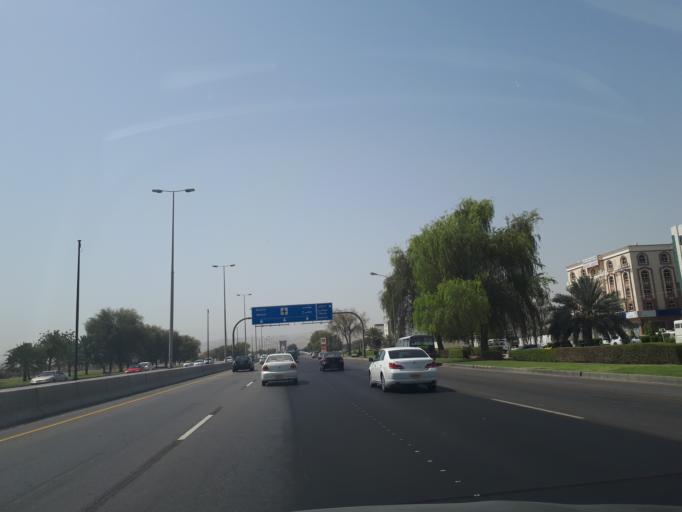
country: OM
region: Muhafazat Masqat
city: As Sib al Jadidah
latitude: 23.5988
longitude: 58.2500
